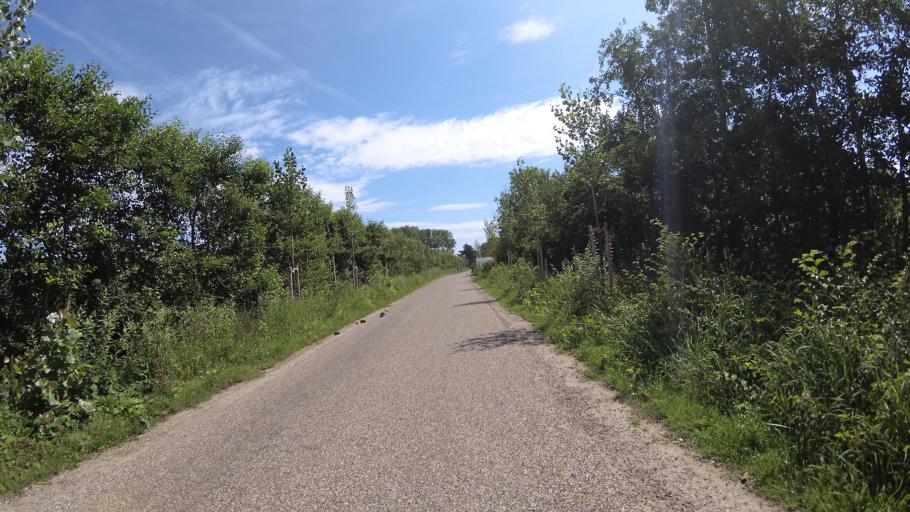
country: NL
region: Zeeland
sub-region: Gemeente Middelburg
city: Middelburg
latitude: 51.5770
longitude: 3.5803
